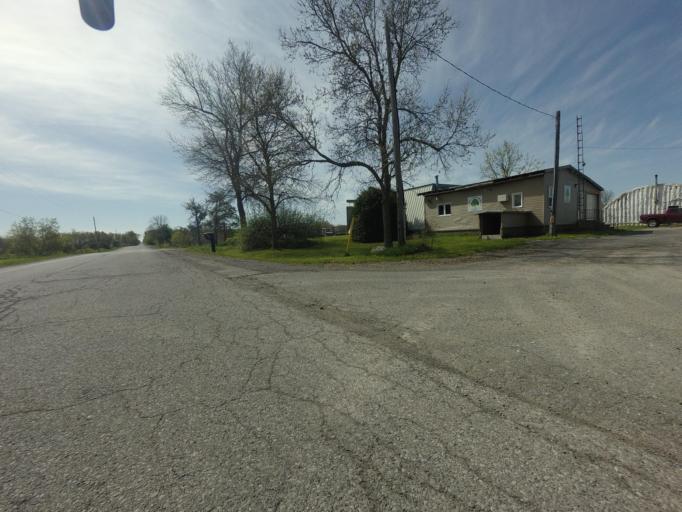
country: CA
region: Ontario
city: Arnprior
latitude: 45.4319
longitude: -76.2408
